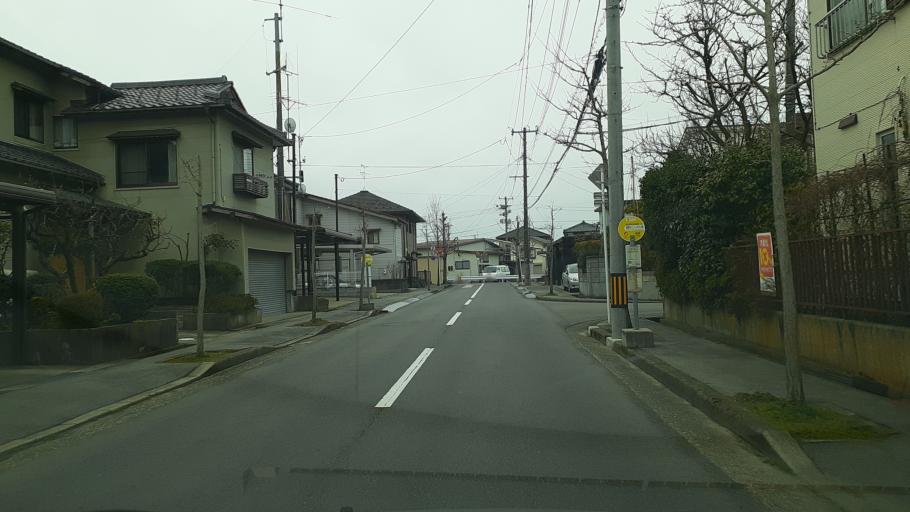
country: JP
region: Niigata
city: Niigata-shi
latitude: 37.8604
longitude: 139.0382
